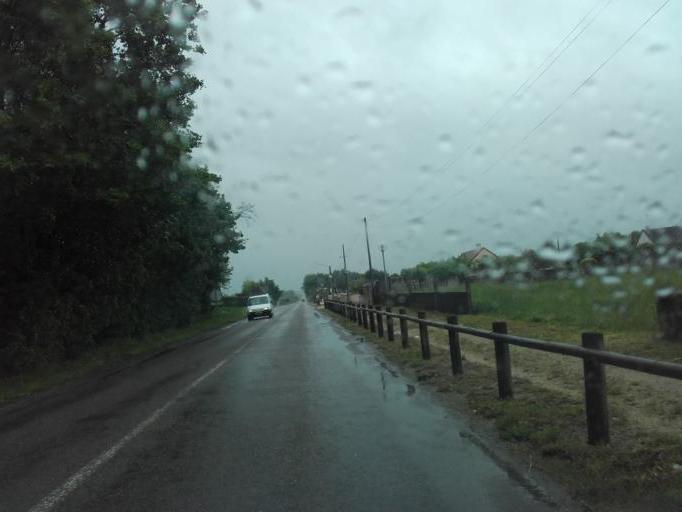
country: FR
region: Bourgogne
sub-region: Departement de Saone-et-Loire
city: Chagny
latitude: 46.8989
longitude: 4.7522
